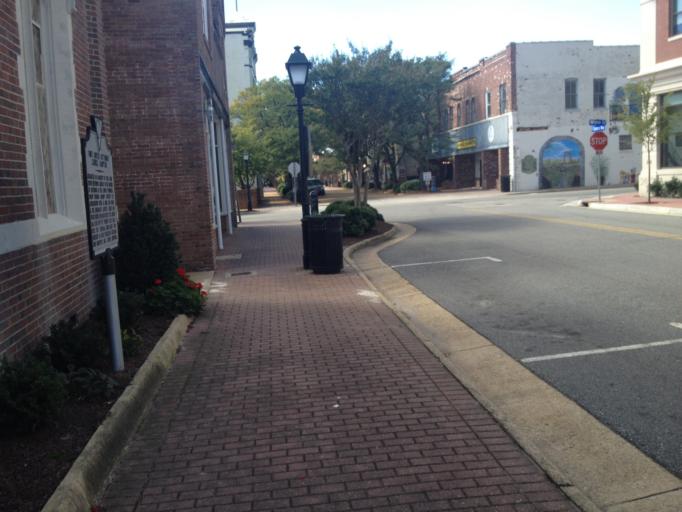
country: US
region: Virginia
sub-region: City of Hampton
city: Hampton
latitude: 37.0259
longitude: -76.3425
